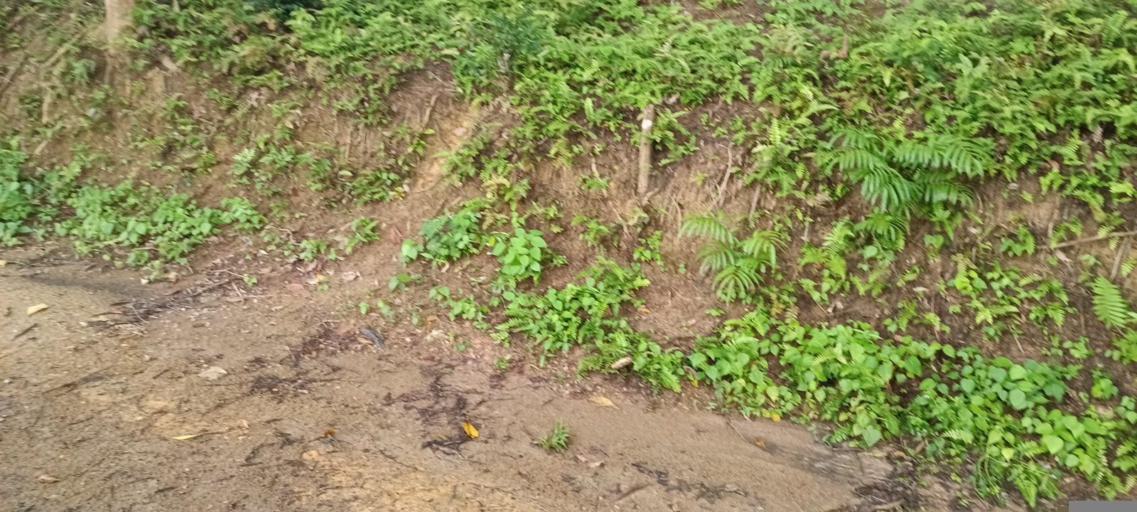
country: MY
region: Penang
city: Juru
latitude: 5.2694
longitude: 100.4150
